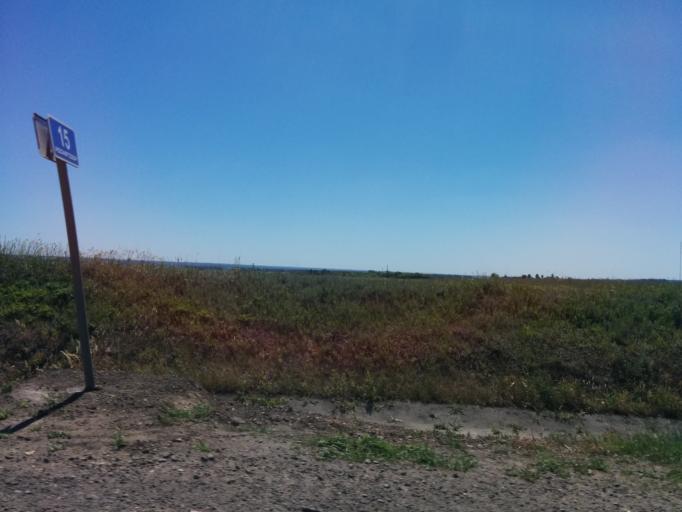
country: RU
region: Tambov
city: Donskoye
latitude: 52.8320
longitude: 41.4144
